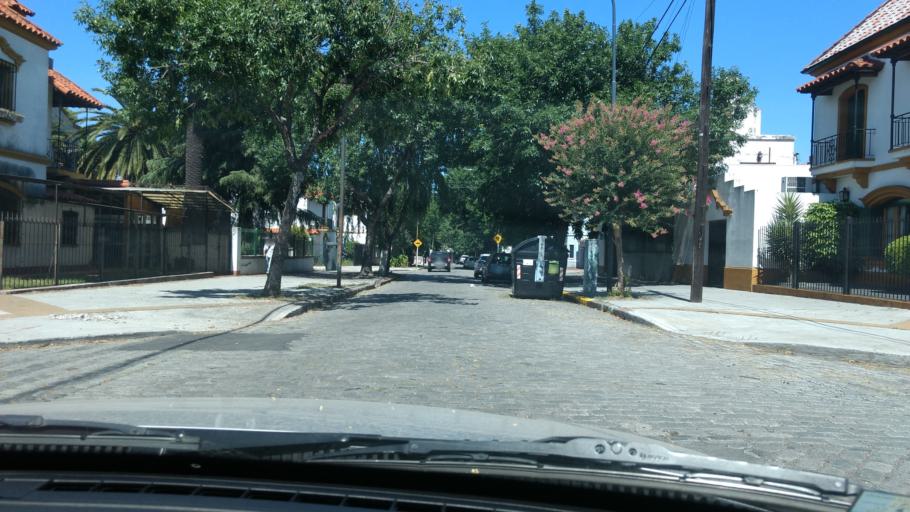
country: AR
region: Buenos Aires
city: Caseros
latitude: -34.6290
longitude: -58.5269
